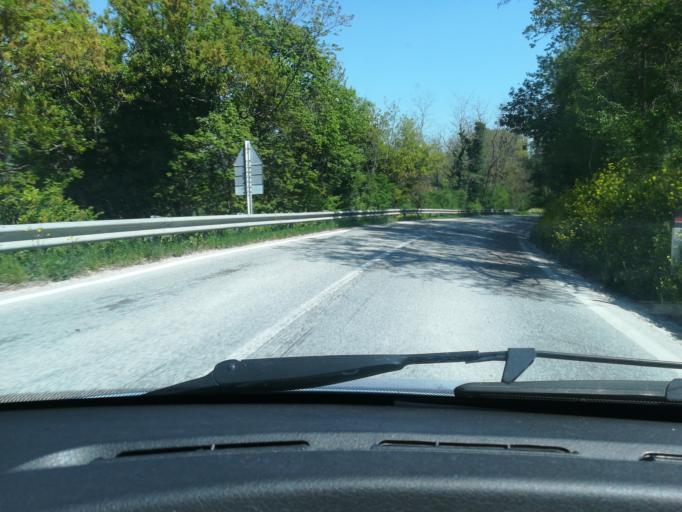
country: IT
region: The Marches
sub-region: Provincia di Macerata
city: Strada
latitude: 43.4067
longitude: 13.2082
